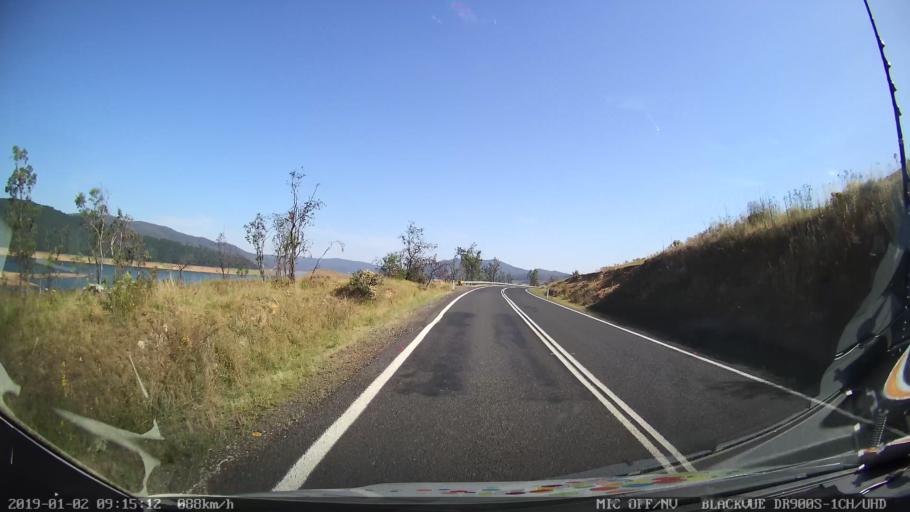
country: AU
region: New South Wales
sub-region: Tumut Shire
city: Tumut
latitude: -35.4680
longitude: 148.2785
